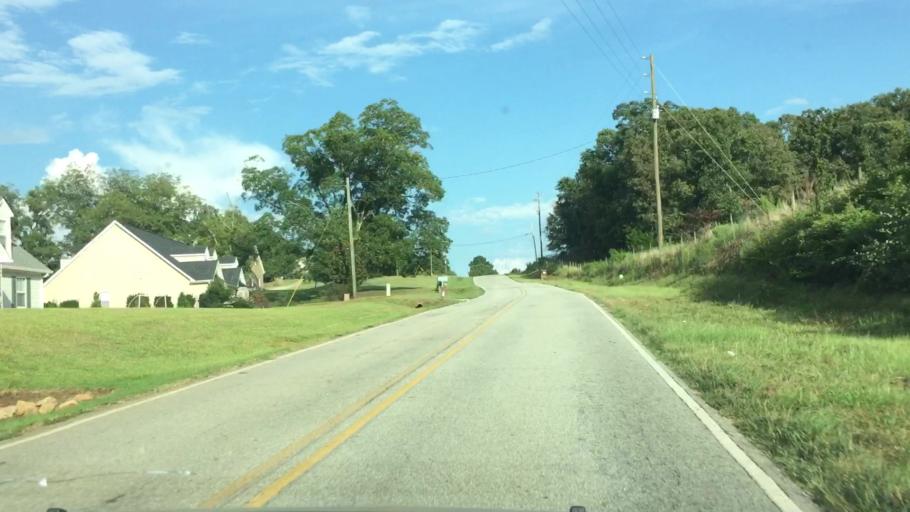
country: US
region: Georgia
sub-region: Newton County
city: Oakwood
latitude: 33.4745
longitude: -84.0234
